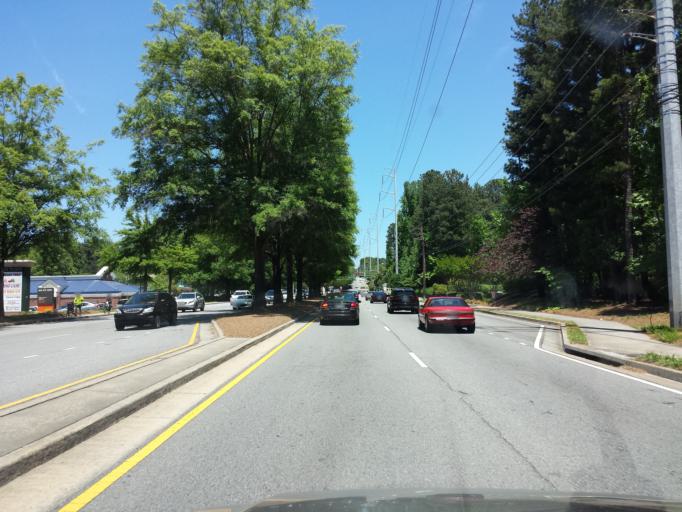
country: US
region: Georgia
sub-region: DeKalb County
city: Dunwoody
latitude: 33.9346
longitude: -84.3377
